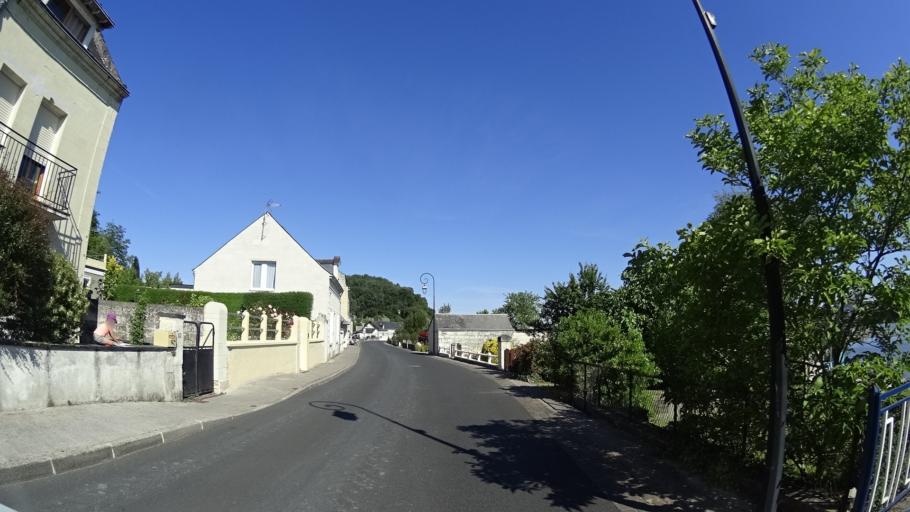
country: FR
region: Pays de la Loire
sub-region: Departement de Maine-et-Loire
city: Chenehutte-Treves-Cunault
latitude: 47.3070
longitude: -0.1509
